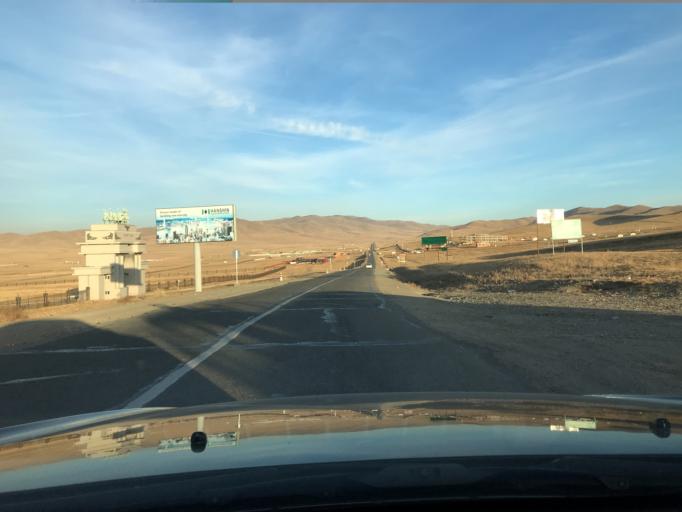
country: MN
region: Central Aimak
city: Arhust
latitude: 47.8046
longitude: 107.5296
